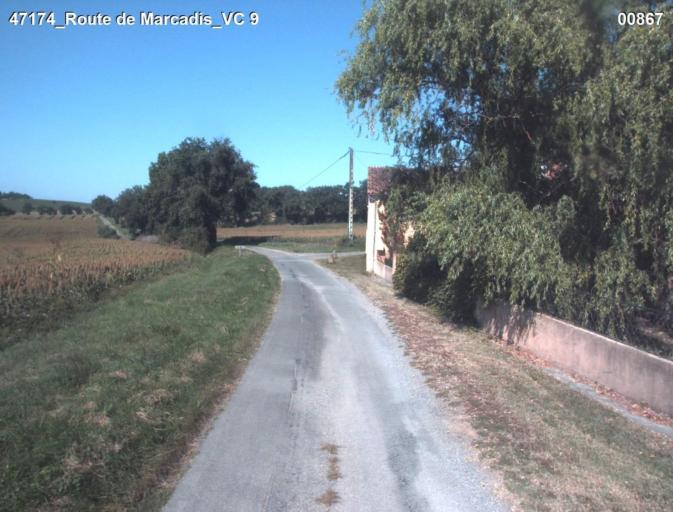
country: FR
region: Midi-Pyrenees
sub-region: Departement du Gers
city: Condom
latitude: 44.0208
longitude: 0.3447
